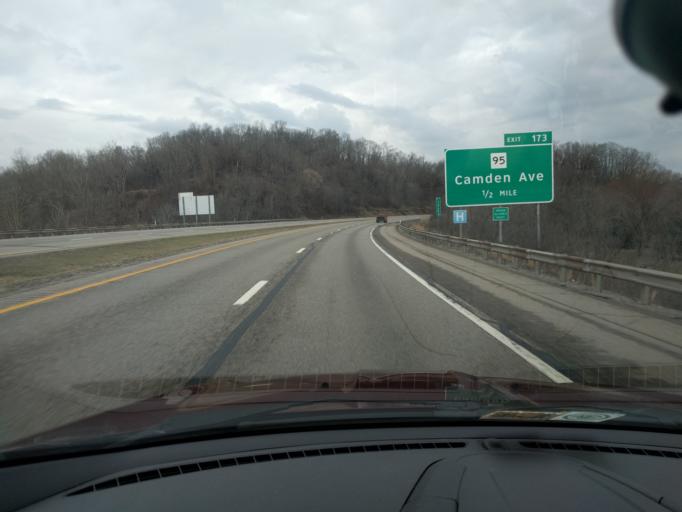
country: US
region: West Virginia
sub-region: Wood County
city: Mineral Wells
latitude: 39.2206
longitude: -81.5273
